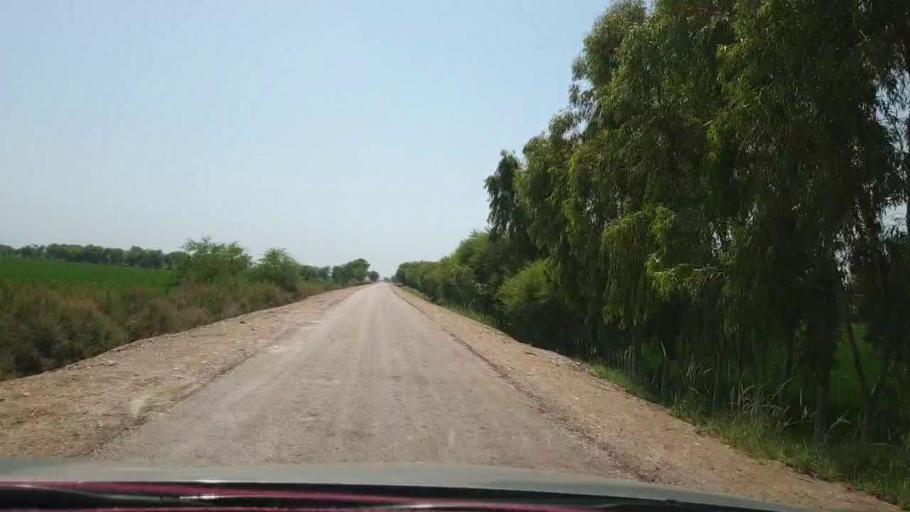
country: PK
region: Sindh
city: Warah
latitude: 27.5393
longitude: 67.7908
